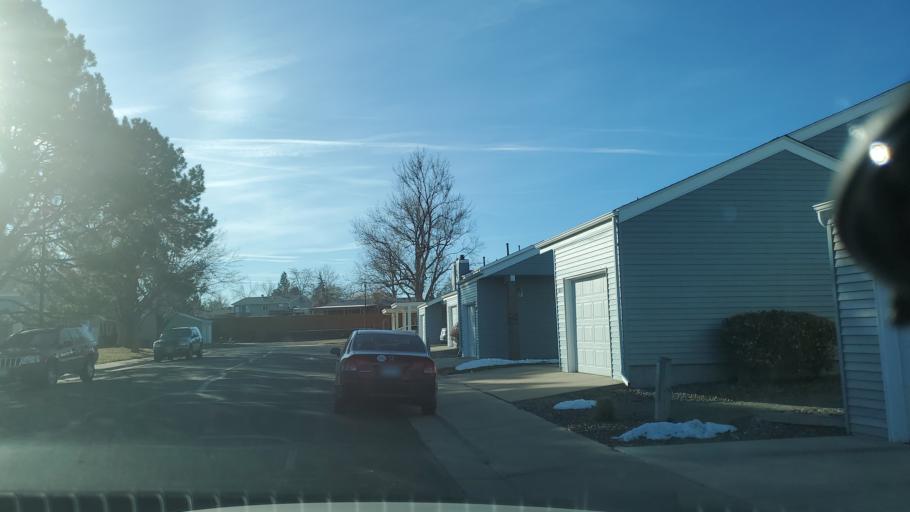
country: US
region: Colorado
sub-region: Adams County
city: Northglenn
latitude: 39.9122
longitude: -104.9452
